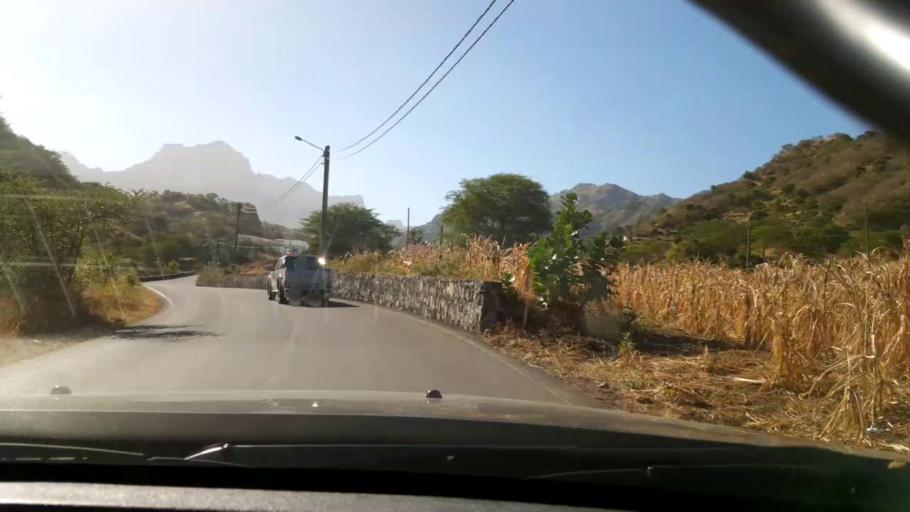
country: CV
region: Sao Lourenco dos Orgaos
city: Joao Teves
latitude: 15.0690
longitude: -23.5759
